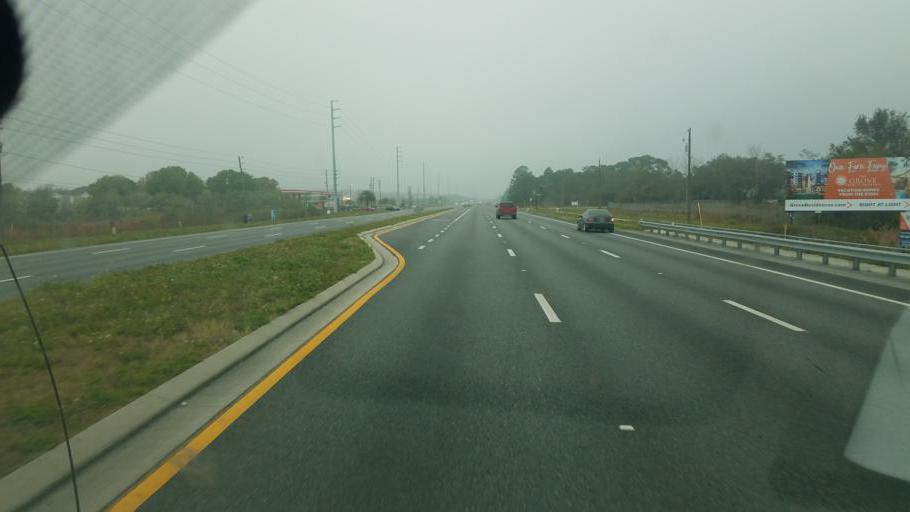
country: US
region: Florida
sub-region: Polk County
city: Citrus Ridge
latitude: 28.3474
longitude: -81.6405
